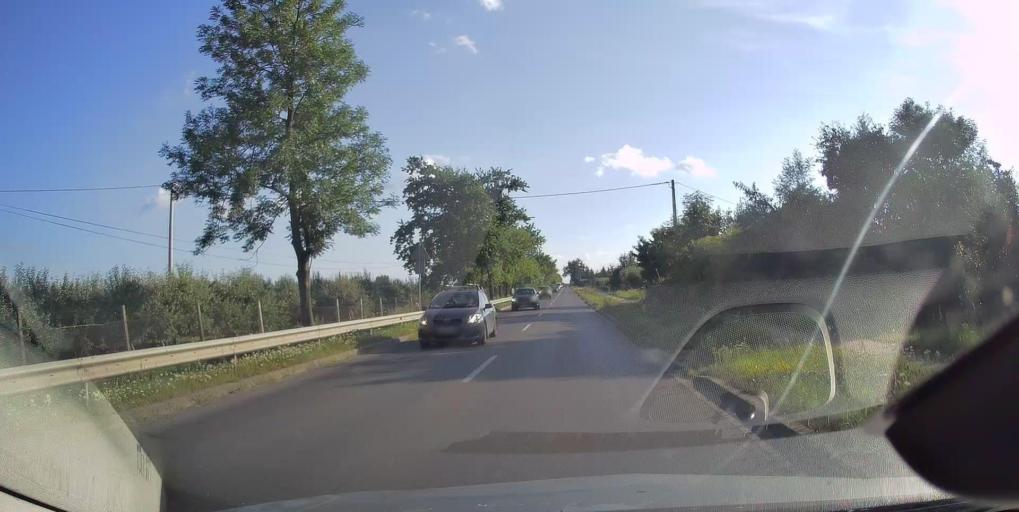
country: PL
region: Masovian Voivodeship
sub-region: Powiat grojecki
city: Belsk Duzy
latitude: 51.8337
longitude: 20.8195
